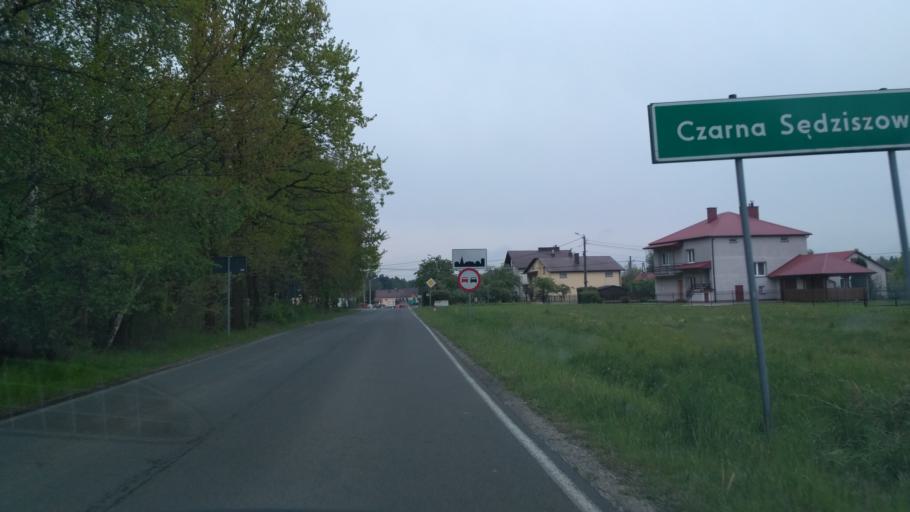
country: PL
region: Subcarpathian Voivodeship
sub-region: Powiat ropczycko-sedziszowski
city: Sedziszow Malopolski
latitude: 50.1274
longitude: 21.7539
